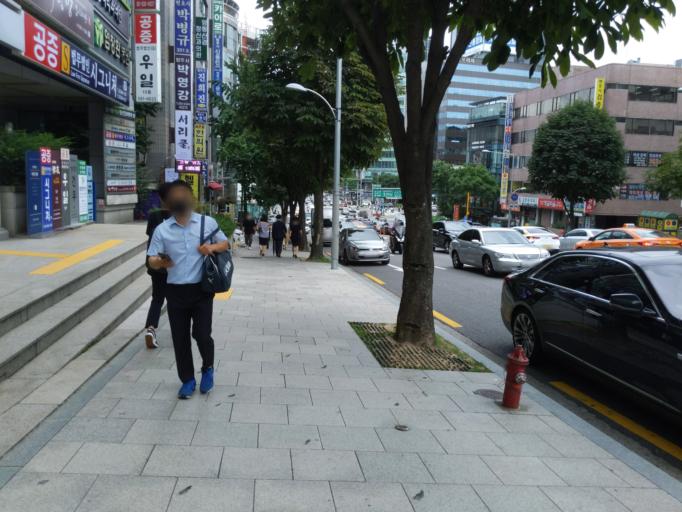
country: KR
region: Seoul
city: Seoul
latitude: 37.4951
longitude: 127.0134
